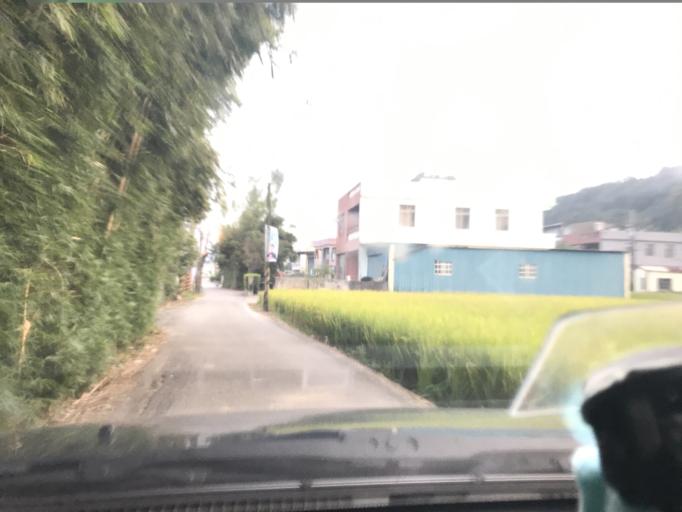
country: TW
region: Taiwan
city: Daxi
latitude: 24.8489
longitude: 121.2097
